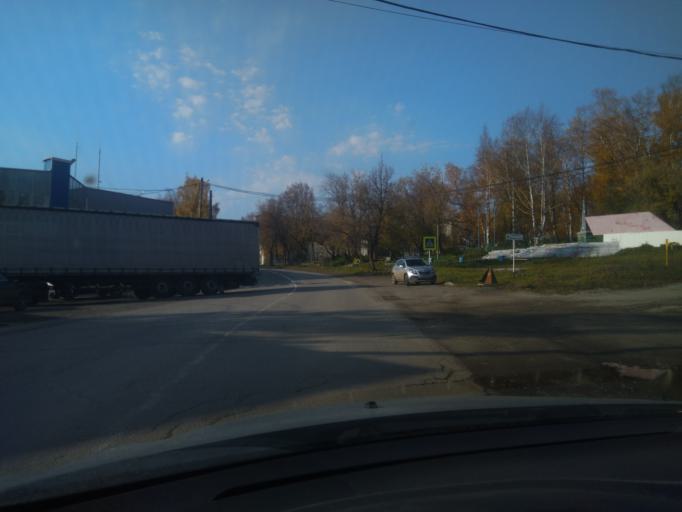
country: RU
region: Sverdlovsk
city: Nizhniye Sergi
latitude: 56.6686
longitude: 59.3193
